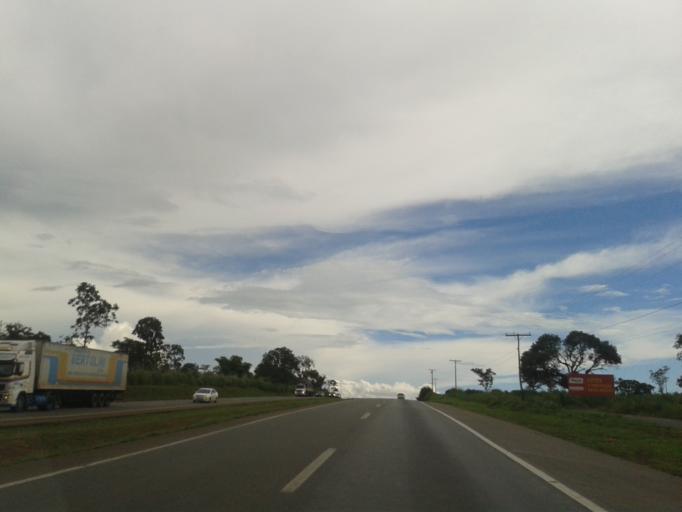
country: BR
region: Goias
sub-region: Aparecida De Goiania
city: Aparecida de Goiania
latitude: -16.8613
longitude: -49.2494
